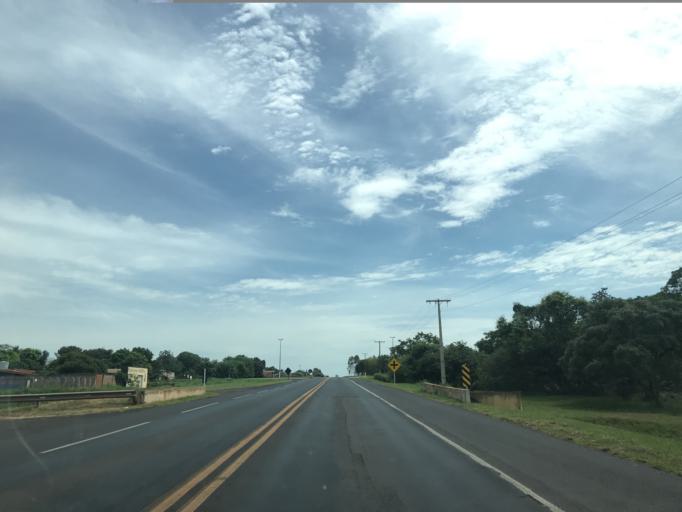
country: BR
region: Sao Paulo
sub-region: Nova Granada
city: Nova Granada
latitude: -20.2898
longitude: -49.2013
